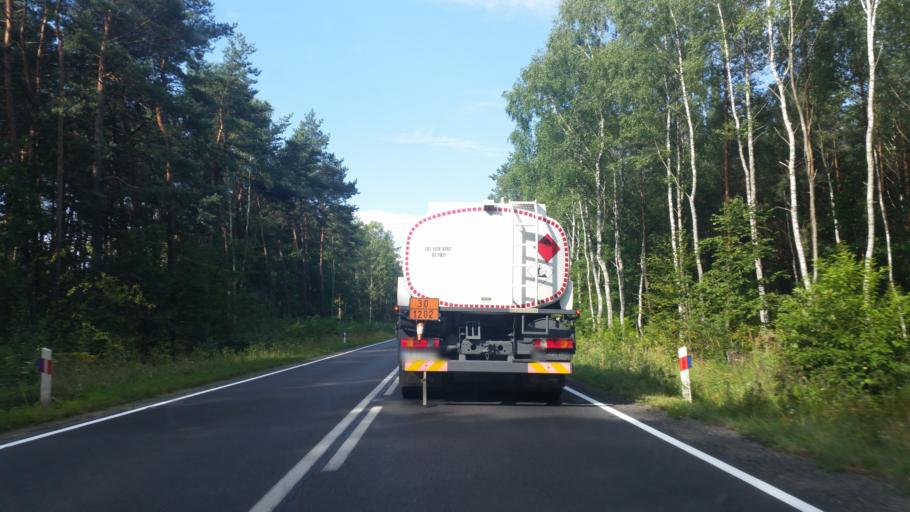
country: PL
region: Lesser Poland Voivodeship
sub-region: Powiat chrzanowski
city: Zarki
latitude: 50.1148
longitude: 19.3525
